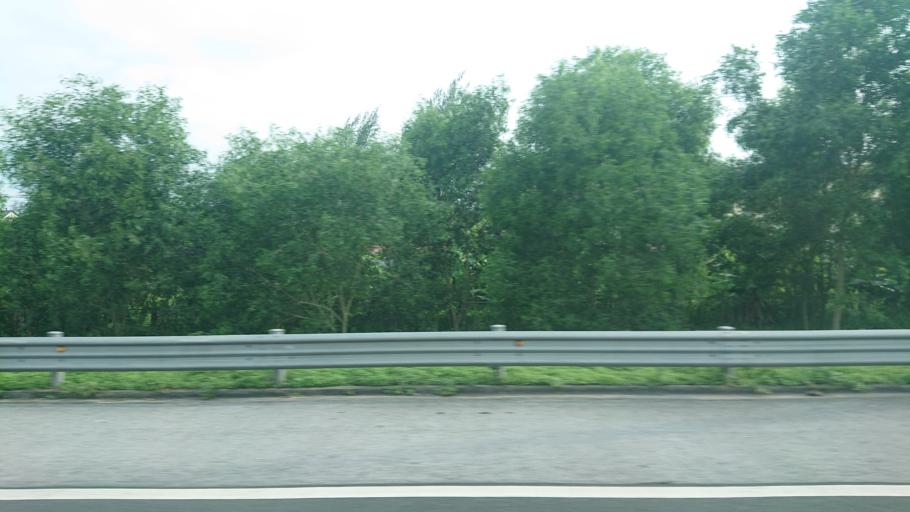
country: VN
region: Hai Phong
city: An Lao
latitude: 20.7860
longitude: 106.5604
